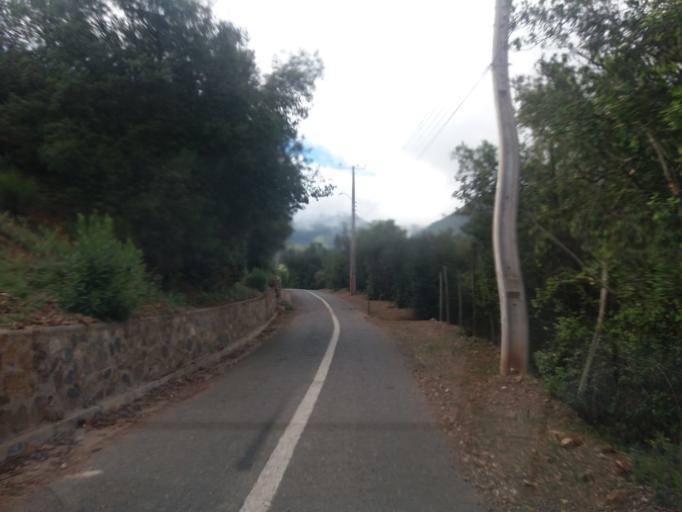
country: CL
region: Valparaiso
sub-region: Provincia de Marga Marga
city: Limache
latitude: -33.0668
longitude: -71.0642
